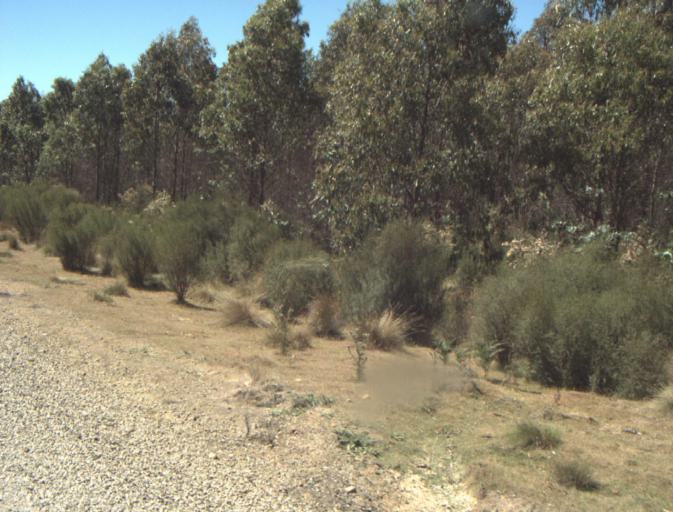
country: AU
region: Tasmania
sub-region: Dorset
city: Scottsdale
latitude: -41.3055
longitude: 147.4670
